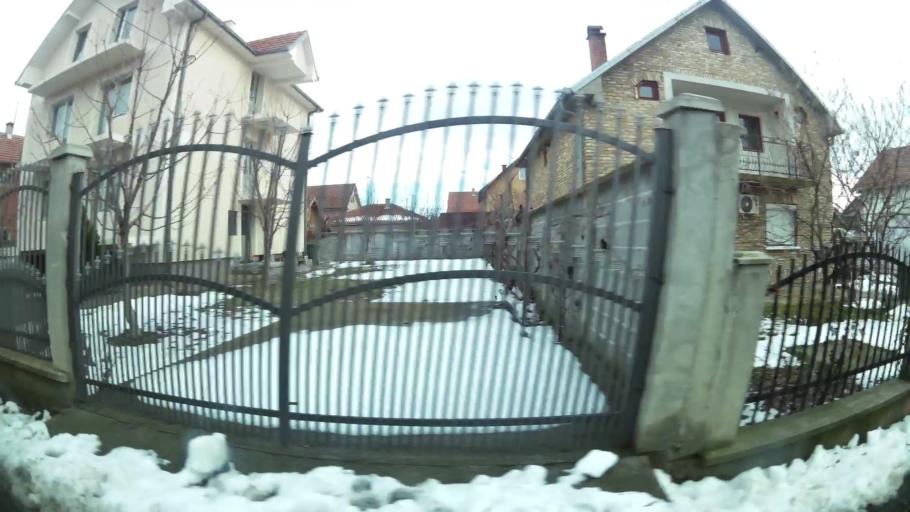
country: RS
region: Central Serbia
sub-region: Belgrade
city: Surcin
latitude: 44.8003
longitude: 20.2966
